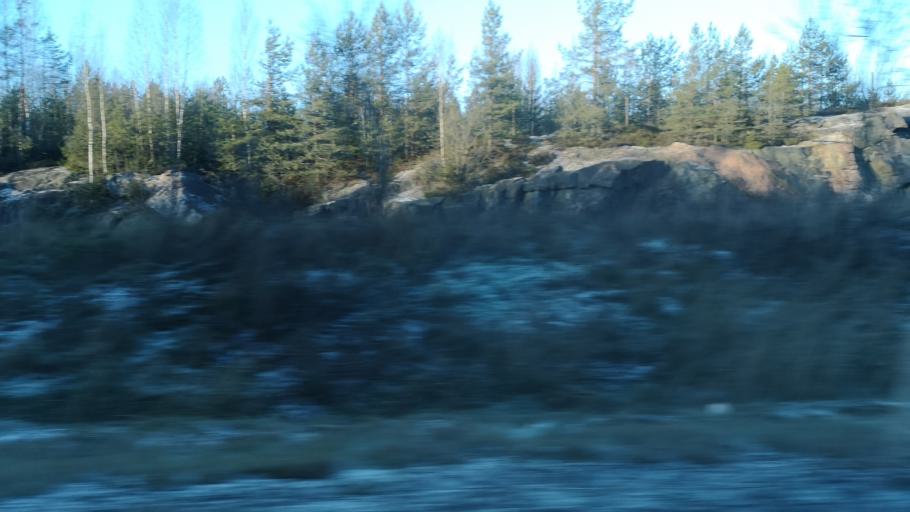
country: FI
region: Uusimaa
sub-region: Porvoo
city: Pukkila
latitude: 60.7411
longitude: 25.4529
